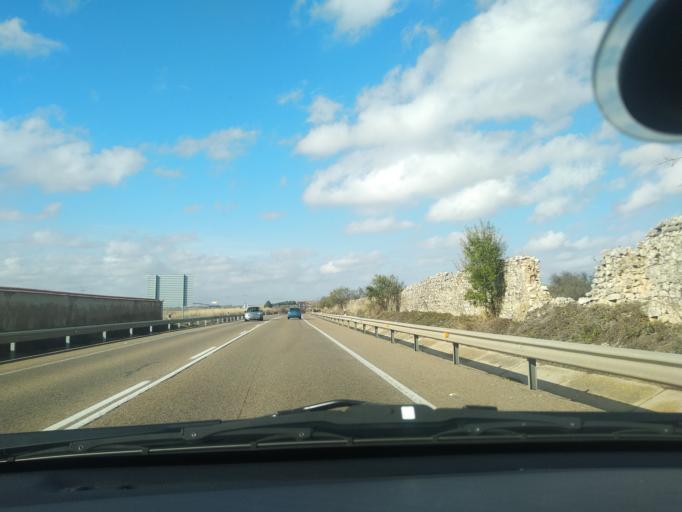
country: ES
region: Castille and Leon
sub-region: Provincia de Valladolid
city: Medina de Rioseco
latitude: 41.8687
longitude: -5.0300
